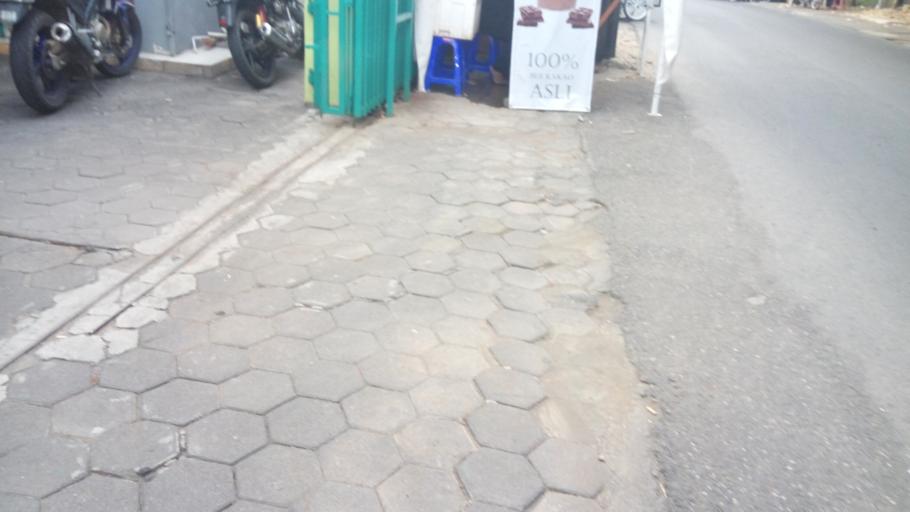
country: ID
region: Central Java
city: Semarang
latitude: -7.0275
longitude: 110.4059
